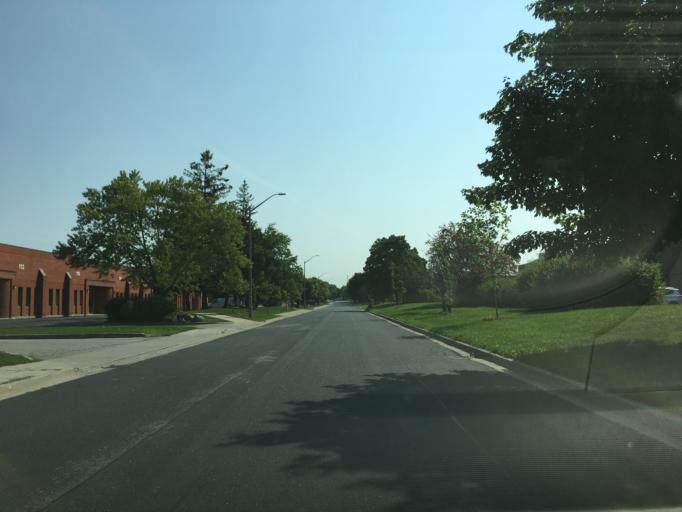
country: CA
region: Ontario
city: Markham
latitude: 43.8242
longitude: -79.3322
